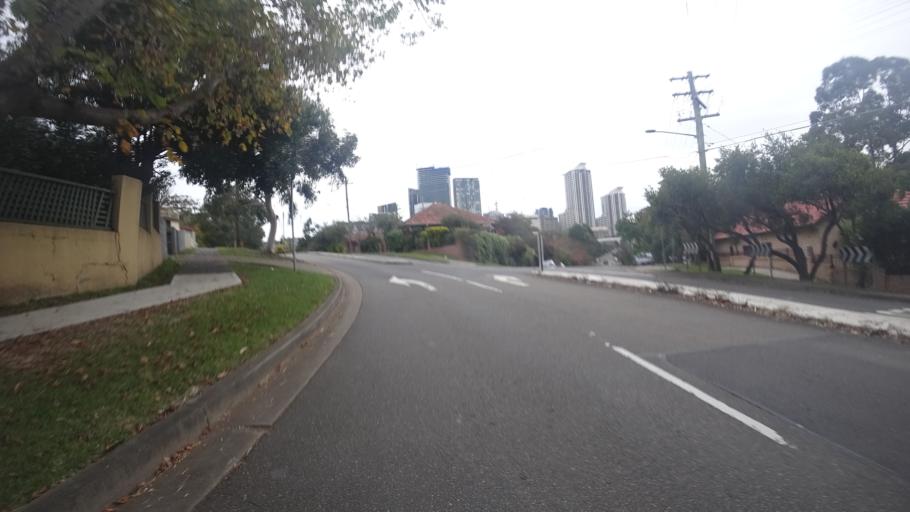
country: AU
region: New South Wales
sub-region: North Sydney
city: St Leonards
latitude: -33.8185
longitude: 151.1979
